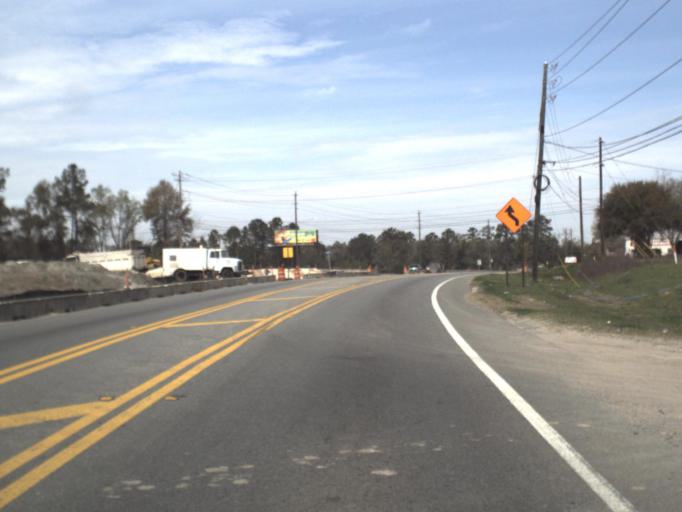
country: US
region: Florida
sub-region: Leon County
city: Tallahassee
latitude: 30.4521
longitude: -84.3597
